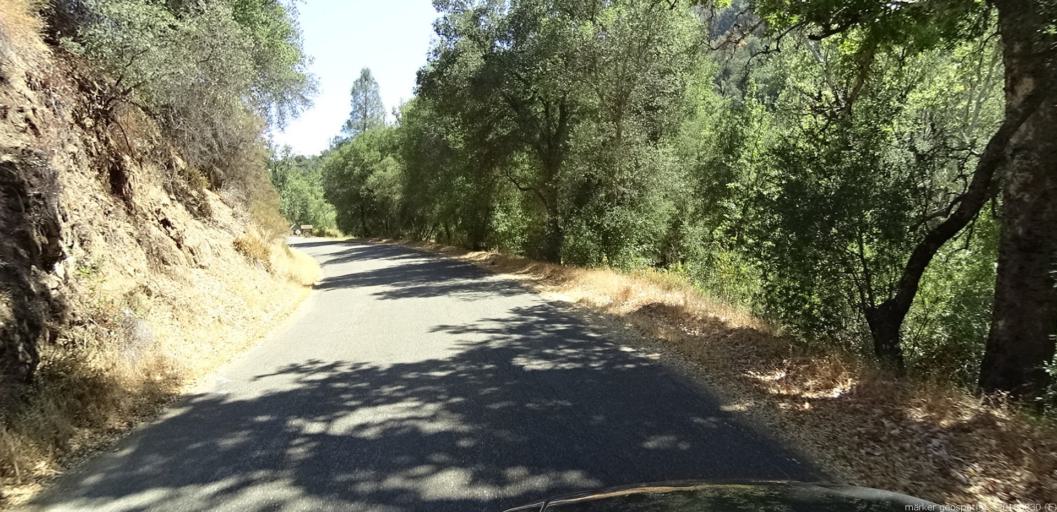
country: US
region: California
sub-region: Monterey County
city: King City
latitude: 35.9980
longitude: -121.3825
